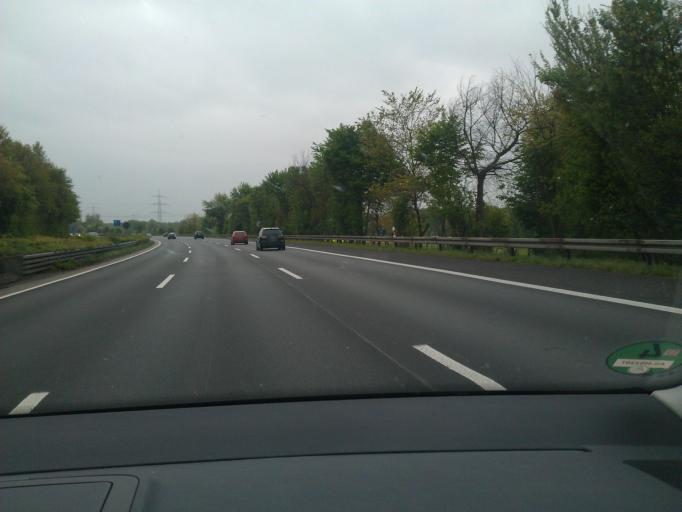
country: DE
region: North Rhine-Westphalia
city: Lohmar
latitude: 50.8396
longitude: 7.2032
